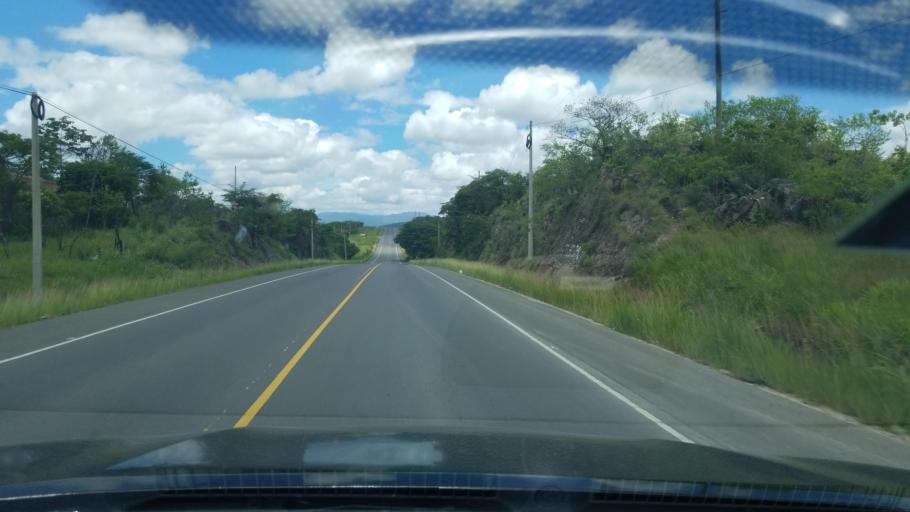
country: HN
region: Francisco Morazan
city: Cofradia
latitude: 14.3012
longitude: -87.2330
